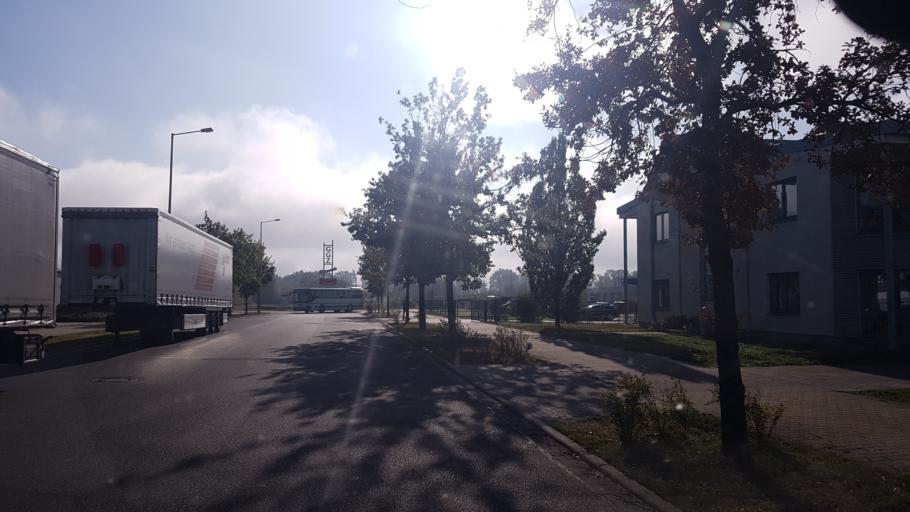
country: DE
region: Brandenburg
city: Elsterwerda
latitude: 51.4614
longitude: 13.5381
